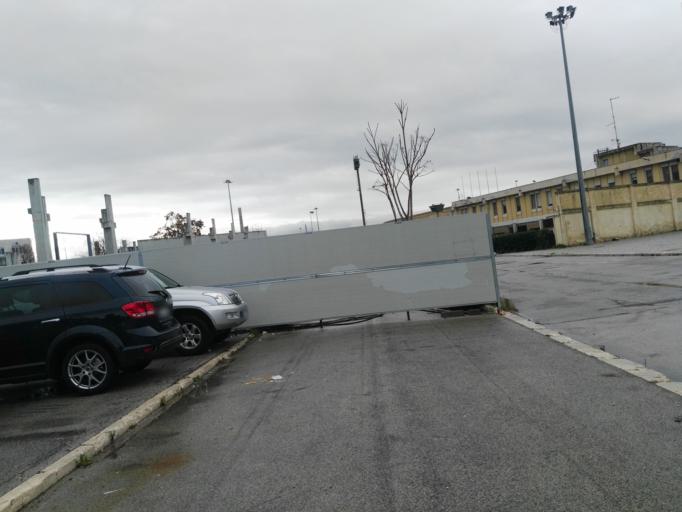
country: IT
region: Apulia
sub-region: Provincia di Bari
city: Bari
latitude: 41.1346
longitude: 16.8414
